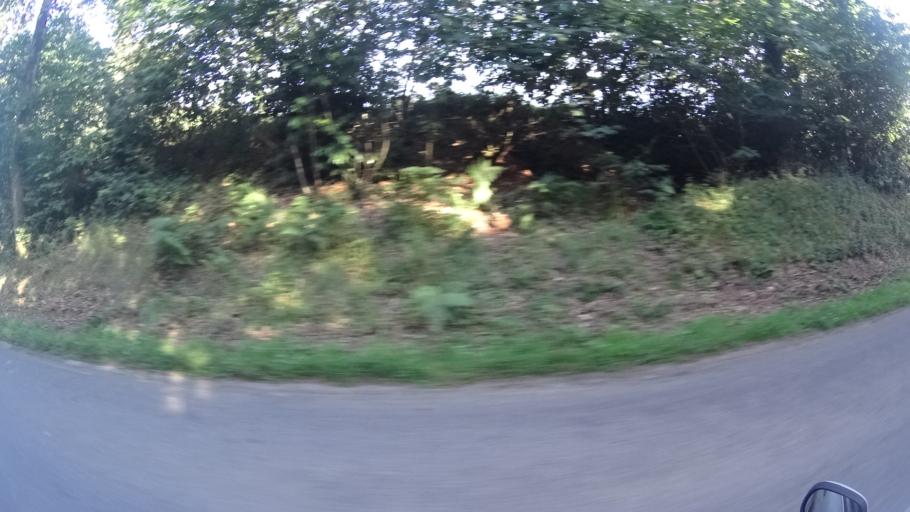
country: FR
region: Brittany
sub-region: Departement du Morbihan
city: Rieux
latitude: 47.6090
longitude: -2.1198
